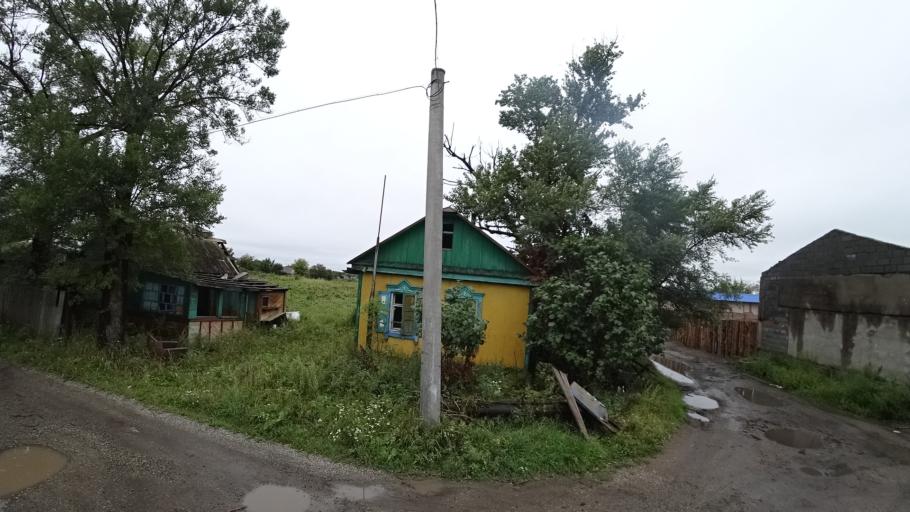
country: RU
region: Primorskiy
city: Monastyrishche
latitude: 44.2086
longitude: 132.4326
